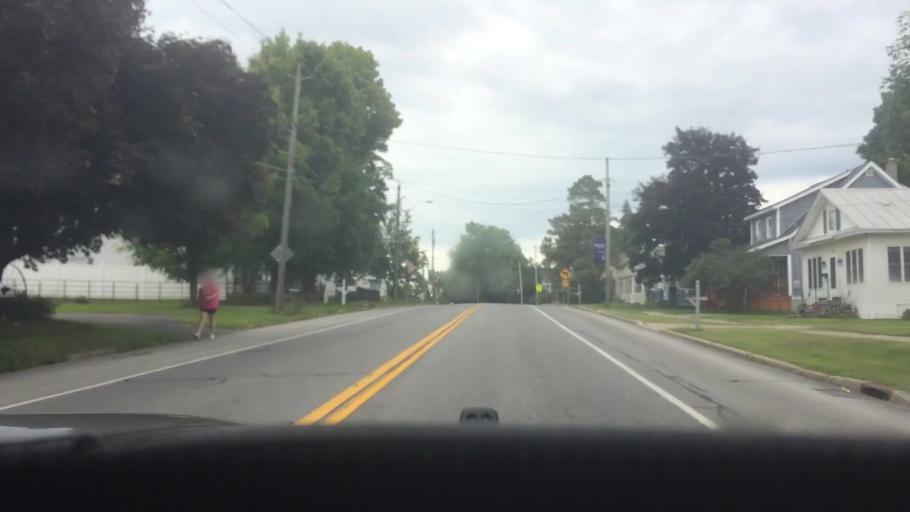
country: US
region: New York
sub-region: St. Lawrence County
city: Ogdensburg
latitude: 44.6220
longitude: -75.4116
